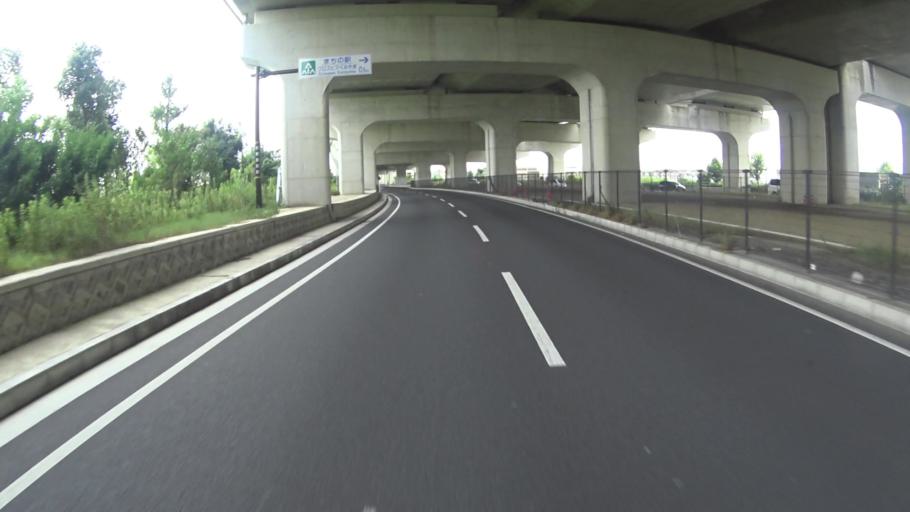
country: JP
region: Kyoto
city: Yawata
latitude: 34.8932
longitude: 135.7497
